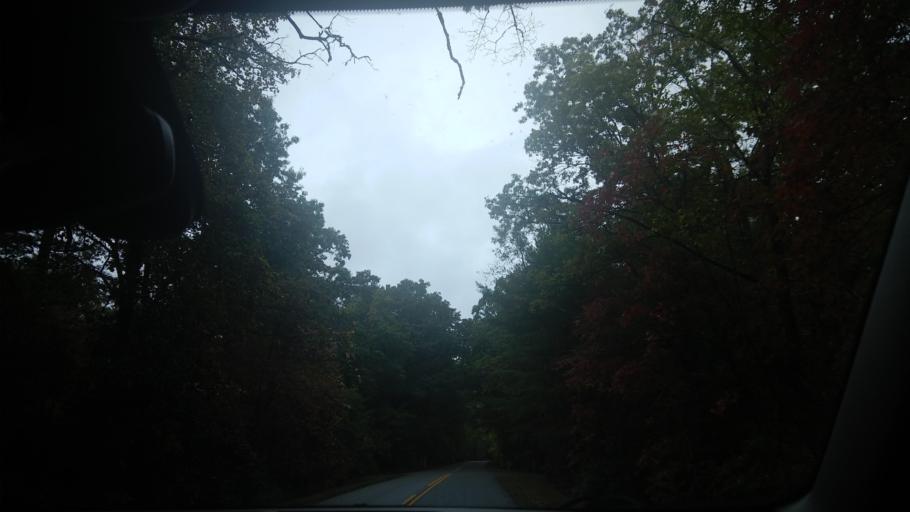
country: US
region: North Carolina
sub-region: Mitchell County
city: Spruce Pine
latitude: 35.8917
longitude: -81.9806
